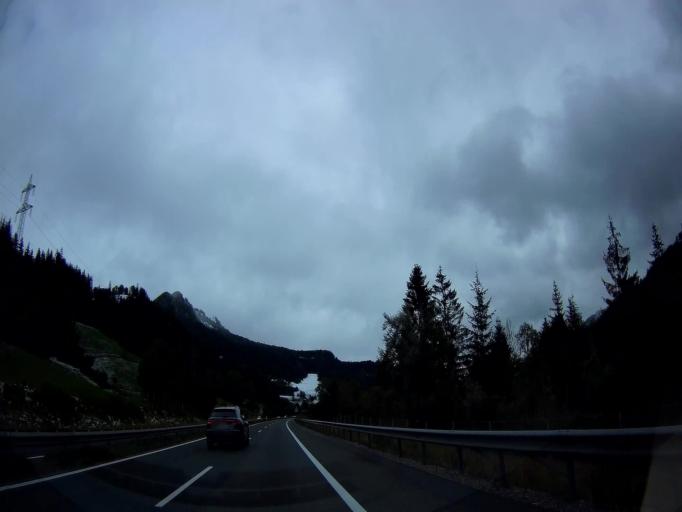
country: AT
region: Styria
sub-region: Politischer Bezirk Leoben
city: Wald am Schoberpass
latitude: 47.4687
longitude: 14.6346
